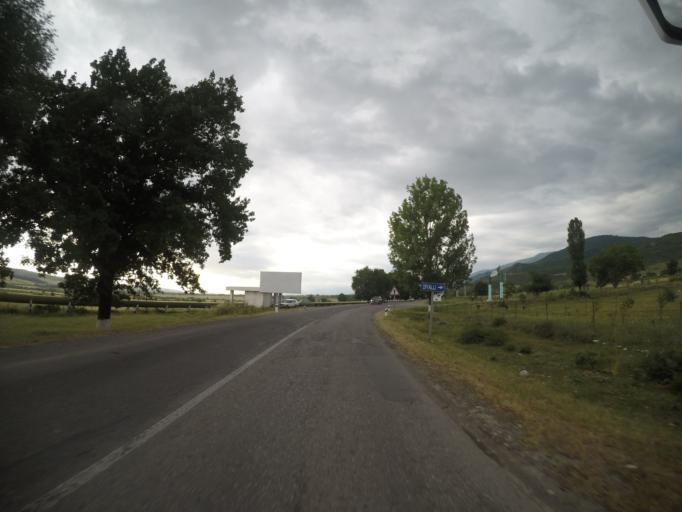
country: AZ
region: Ismayilli
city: Ismayilli
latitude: 40.7607
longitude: 48.2136
